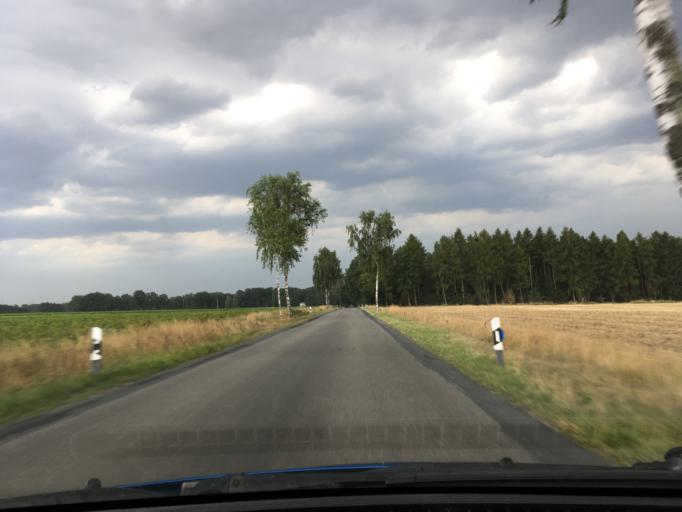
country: DE
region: Lower Saxony
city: Hanstedt Eins
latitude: 53.0616
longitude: 10.3840
